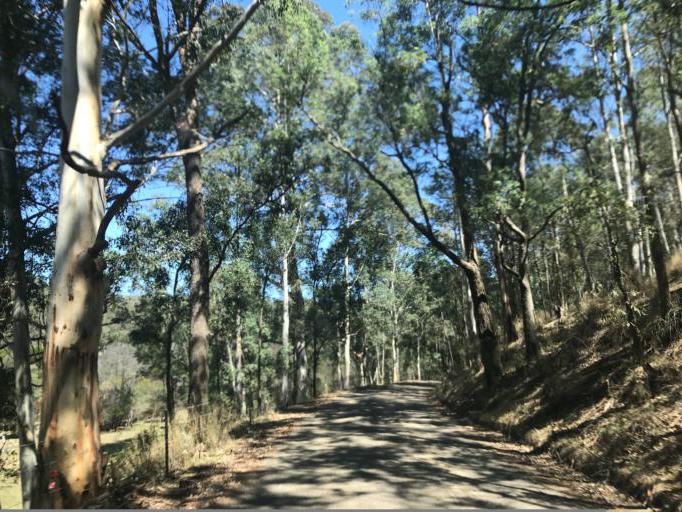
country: AU
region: New South Wales
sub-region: Wyong Shire
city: Little Jilliby
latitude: -33.1997
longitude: 150.9978
